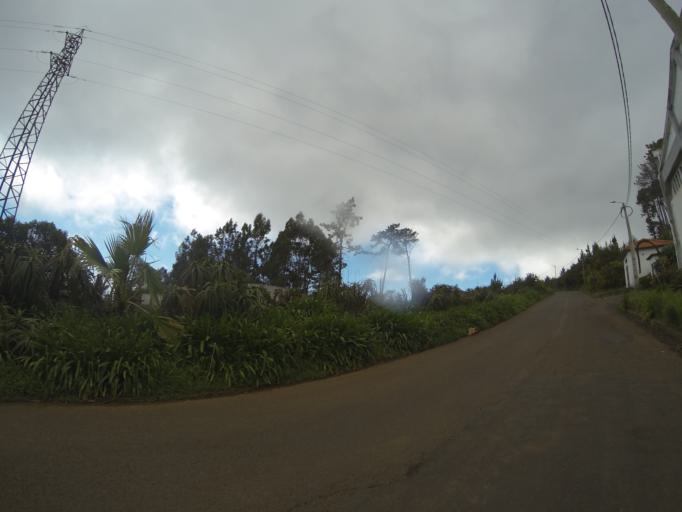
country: PT
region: Madeira
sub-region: Calheta
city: Estreito da Calheta
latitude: 32.7605
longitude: -17.1966
